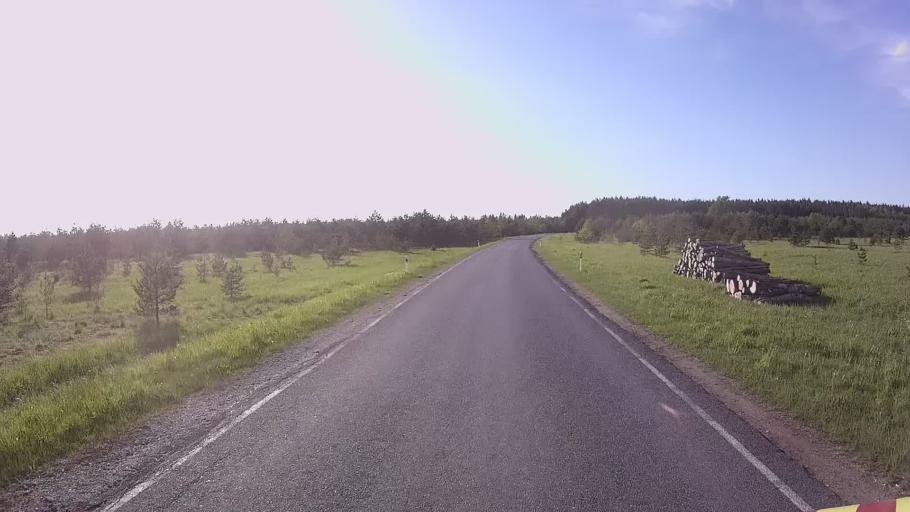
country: EE
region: Laeaene-Virumaa
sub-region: Vinni vald
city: Vinni
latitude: 59.2776
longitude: 26.6070
